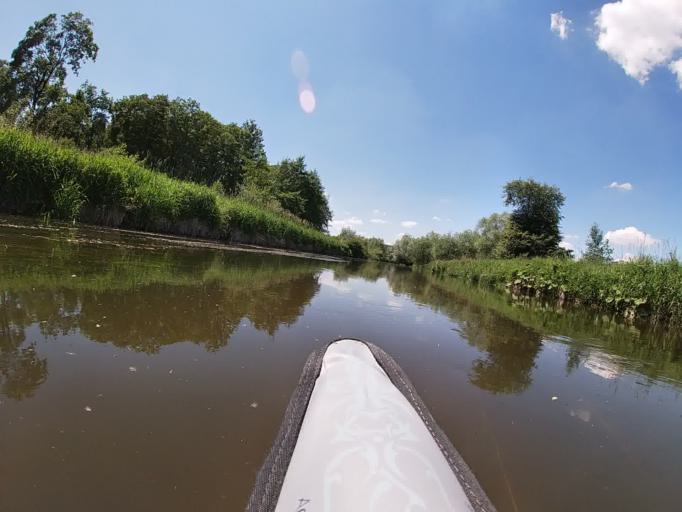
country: DE
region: Bavaria
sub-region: Upper Bavaria
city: Ramerberg
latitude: 48.0205
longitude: 12.1617
